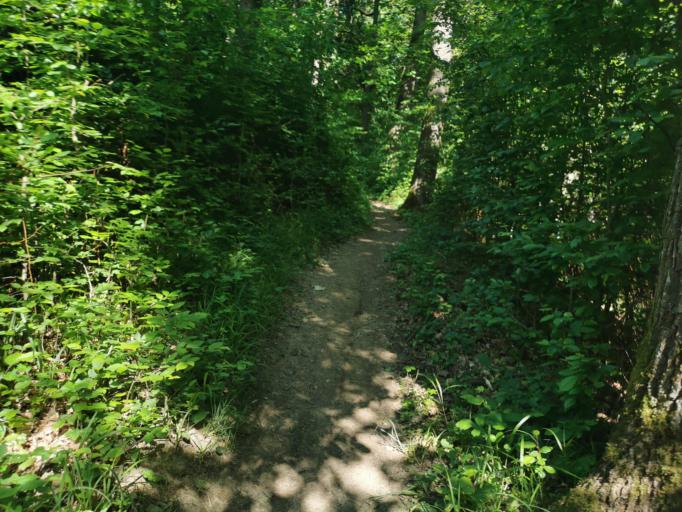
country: CZ
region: South Moravian
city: Knezdub
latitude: 48.8416
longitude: 17.3494
